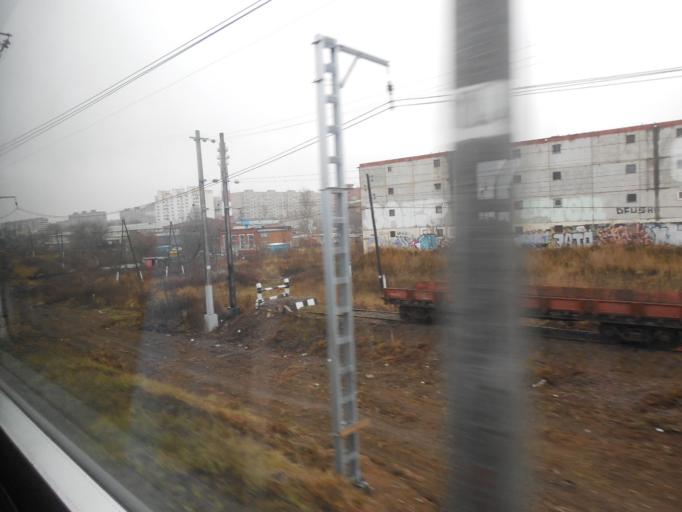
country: RU
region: Moskovskaya
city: Domodedovo
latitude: 55.4339
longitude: 37.7771
